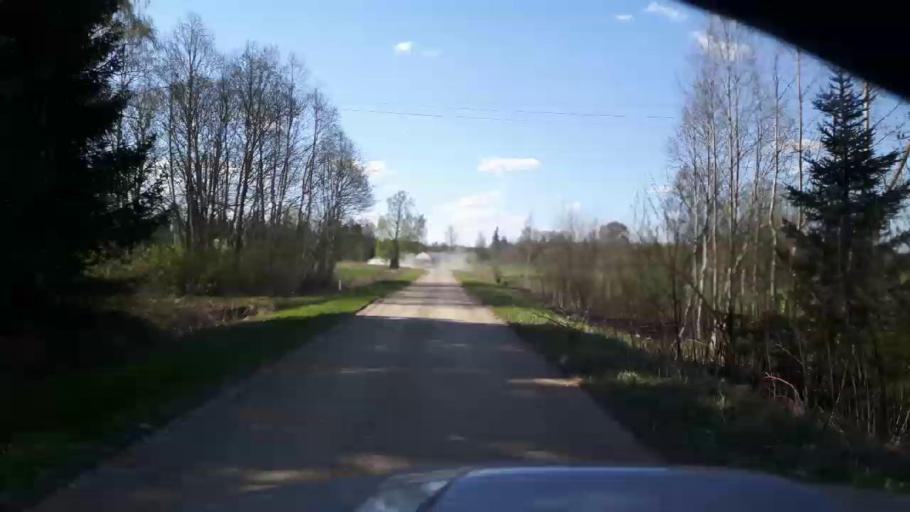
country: EE
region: Paernumaa
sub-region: Tootsi vald
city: Tootsi
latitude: 58.4481
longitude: 24.8637
